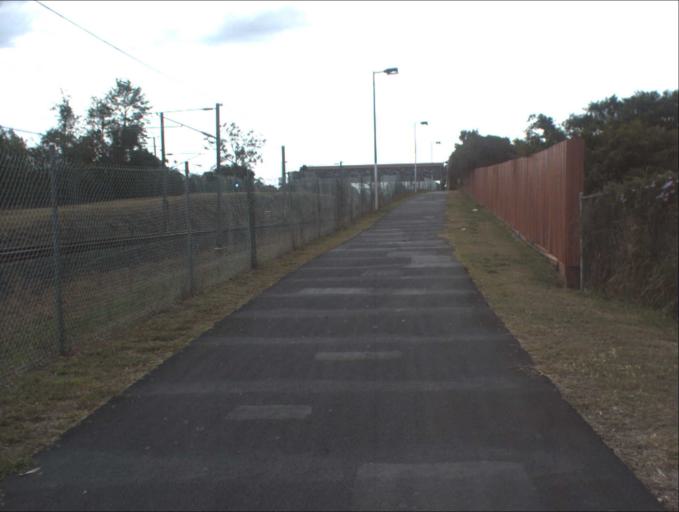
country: AU
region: Queensland
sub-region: Logan
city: Beenleigh
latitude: -27.7062
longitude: 153.1831
